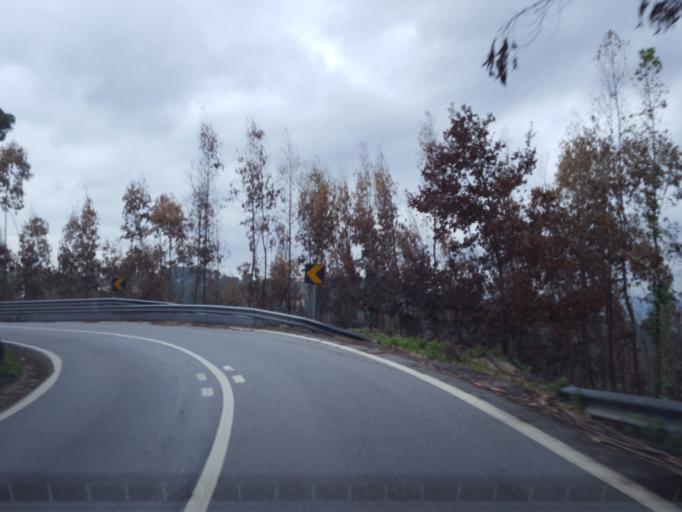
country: PT
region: Porto
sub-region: Marco de Canaveses
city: Marco de Canavezes
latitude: 41.1566
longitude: -8.1376
